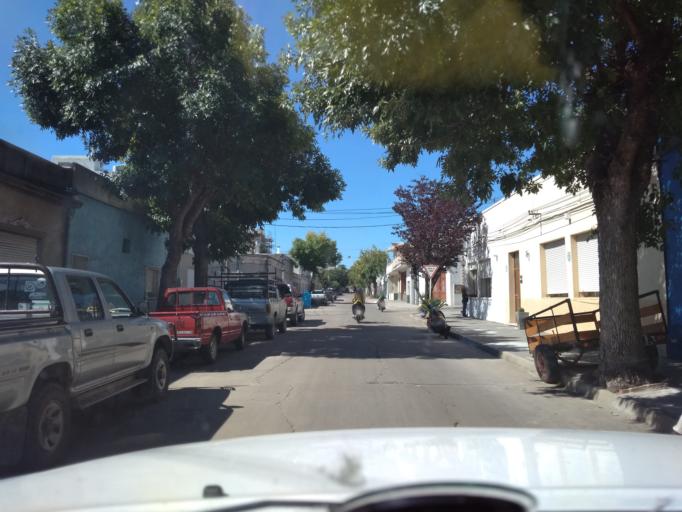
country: UY
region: Florida
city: Florida
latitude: -34.1007
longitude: -56.2181
